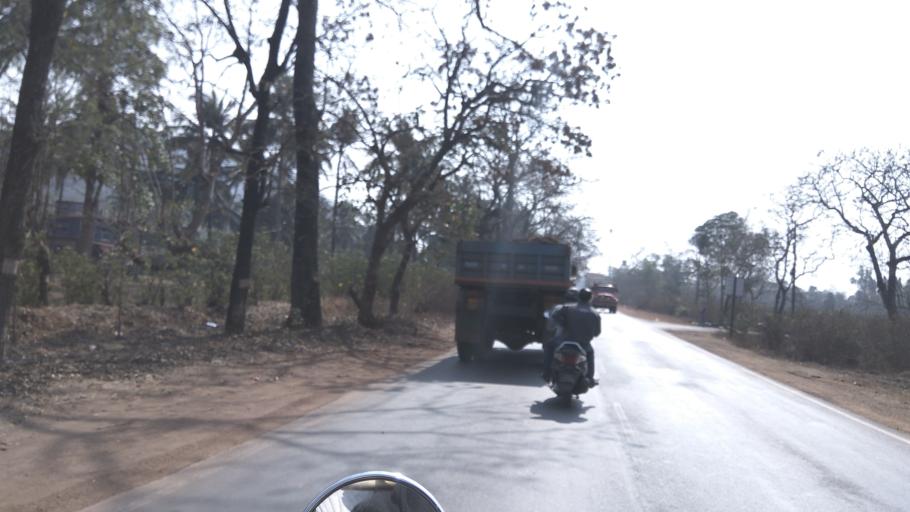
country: IN
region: Goa
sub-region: North Goa
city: Palle
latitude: 15.4053
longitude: 74.0929
